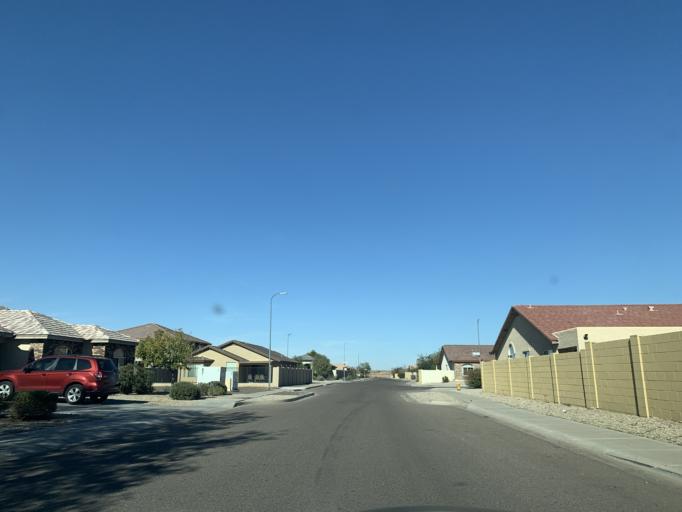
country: US
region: Arizona
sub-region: Maricopa County
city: Laveen
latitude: 33.3960
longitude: -112.1220
